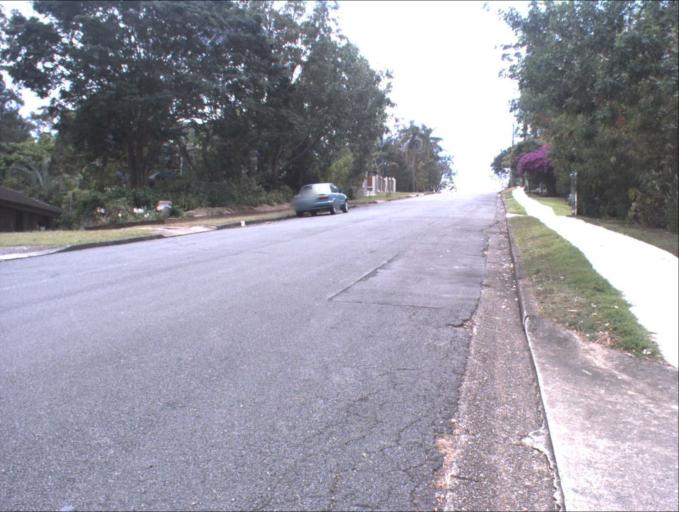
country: AU
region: Queensland
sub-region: Logan
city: Slacks Creek
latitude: -27.6645
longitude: 153.1630
